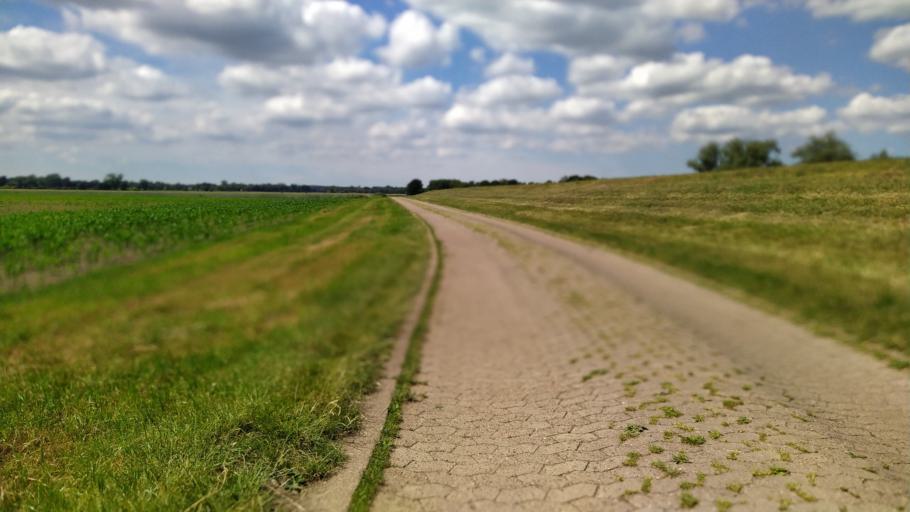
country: DE
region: Lower Saxony
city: Estorf
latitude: 53.5673
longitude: 9.1707
